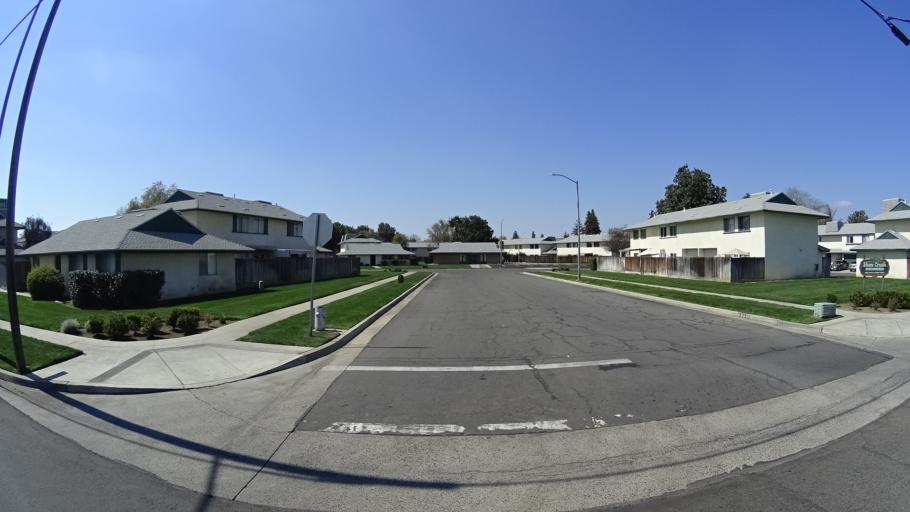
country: US
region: California
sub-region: Fresno County
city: Tarpey Village
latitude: 36.8058
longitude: -119.7320
